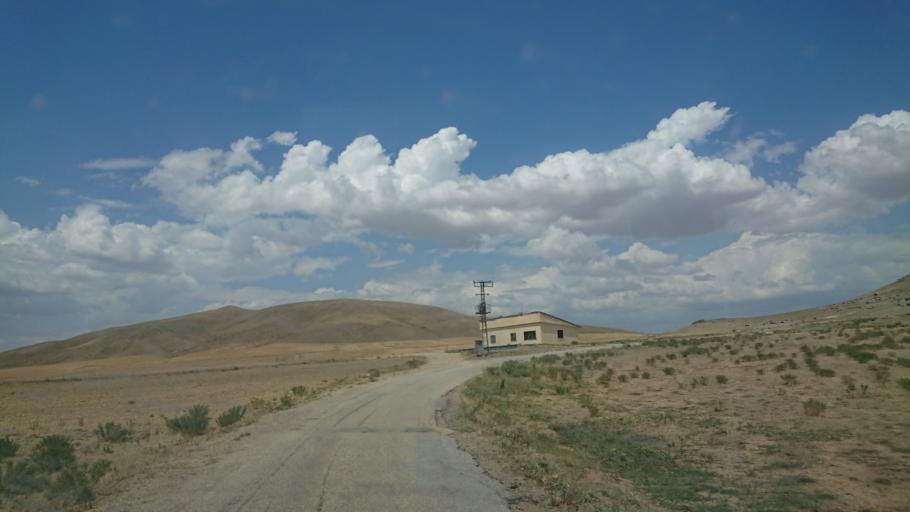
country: TR
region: Aksaray
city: Sariyahsi
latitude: 39.0046
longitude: 33.9103
